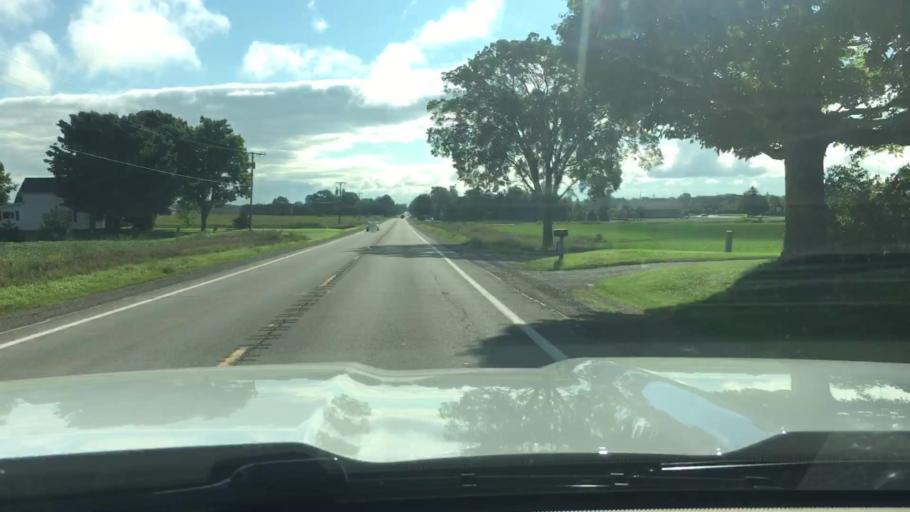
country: US
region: Michigan
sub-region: Tuscola County
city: Cass City
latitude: 43.6004
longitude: -83.2016
